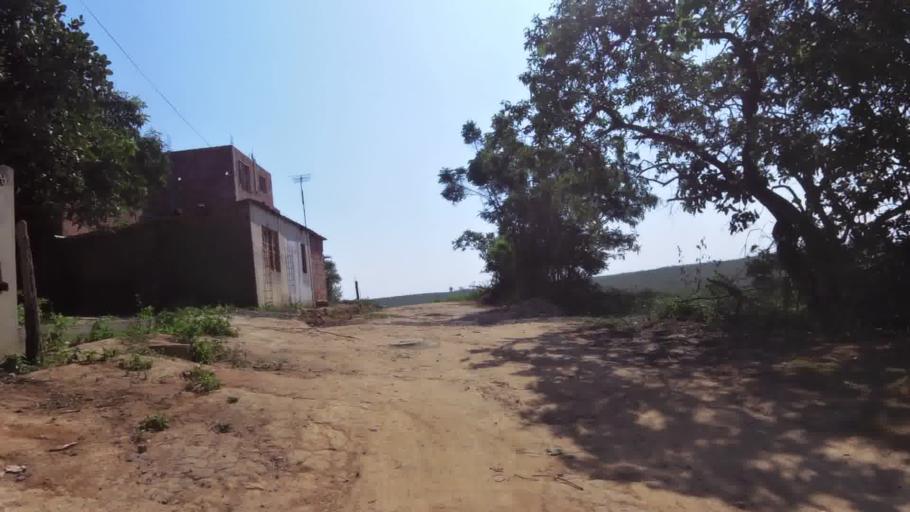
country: BR
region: Espirito Santo
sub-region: Marataizes
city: Marataizes
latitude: -21.0304
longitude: -40.8247
